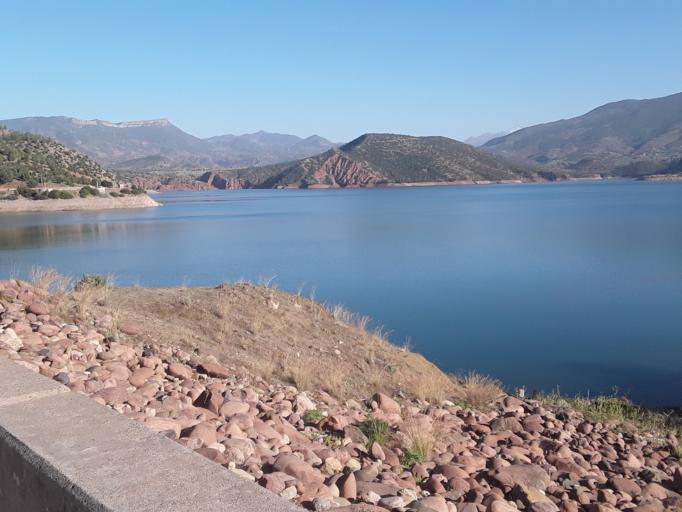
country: MA
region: Marrakech-Tensift-Al Haouz
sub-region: Al-Haouz
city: Abadou
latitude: 31.6451
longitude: -7.2649
